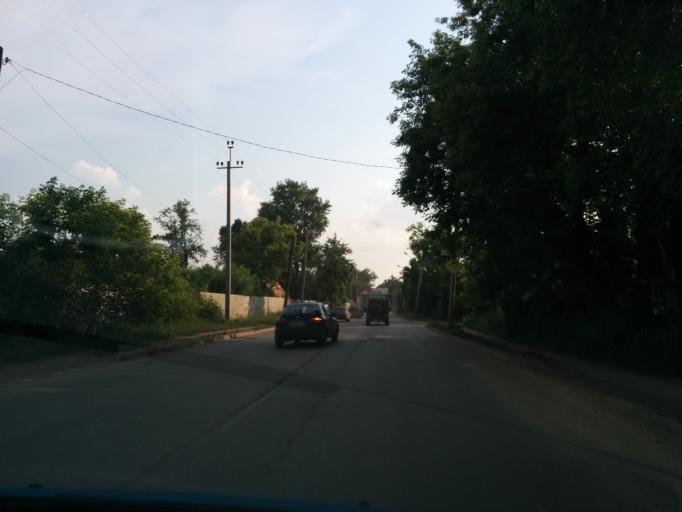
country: RU
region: Perm
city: Perm
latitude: 58.0389
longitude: 56.3149
